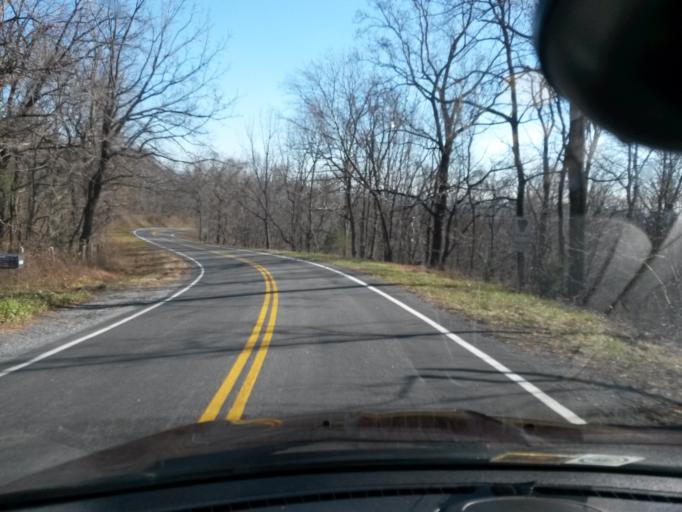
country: US
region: Virginia
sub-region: City of Bedford
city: Bedford
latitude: 37.4338
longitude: -79.5773
